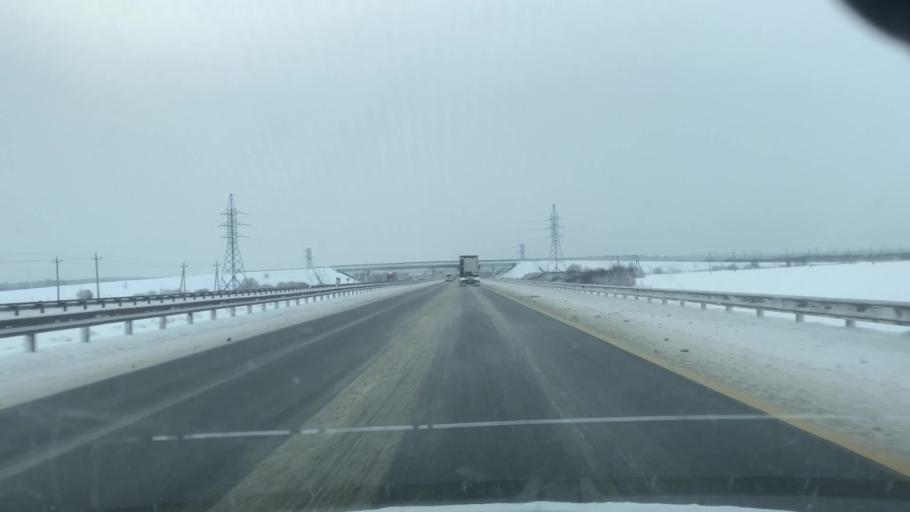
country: RU
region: Moskovskaya
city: Mikhnevo
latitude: 55.1026
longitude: 37.9270
